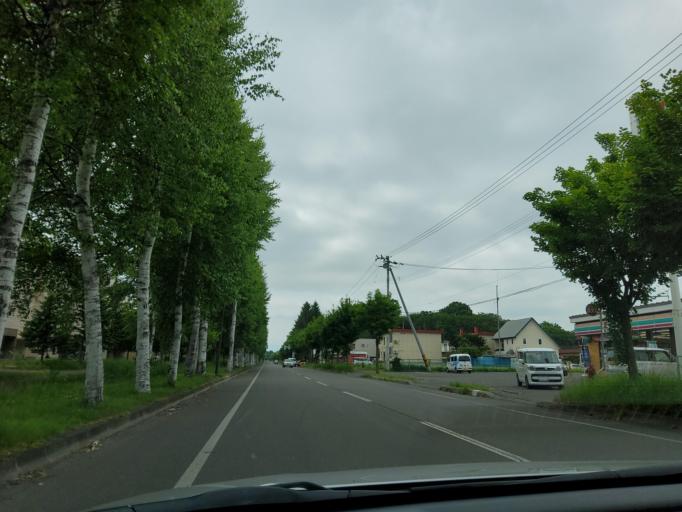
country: JP
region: Hokkaido
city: Obihiro
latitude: 42.9124
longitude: 143.1403
